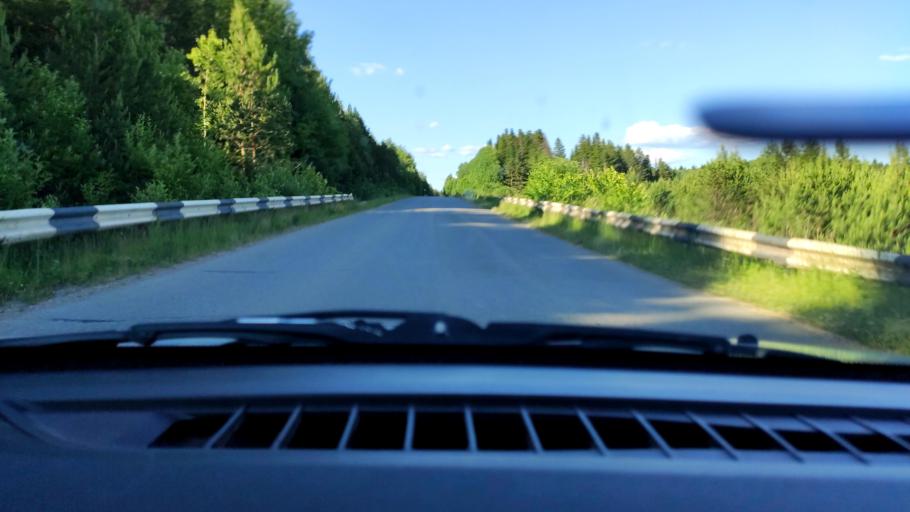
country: RU
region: Perm
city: Uinskoye
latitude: 57.0804
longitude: 56.6133
